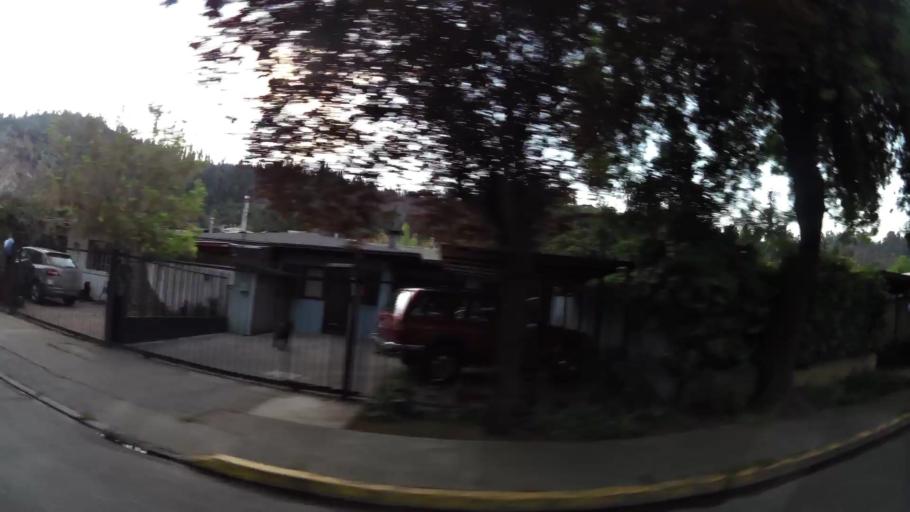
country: CL
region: Santiago Metropolitan
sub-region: Provincia de Santiago
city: Santiago
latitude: -33.4184
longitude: -70.6189
